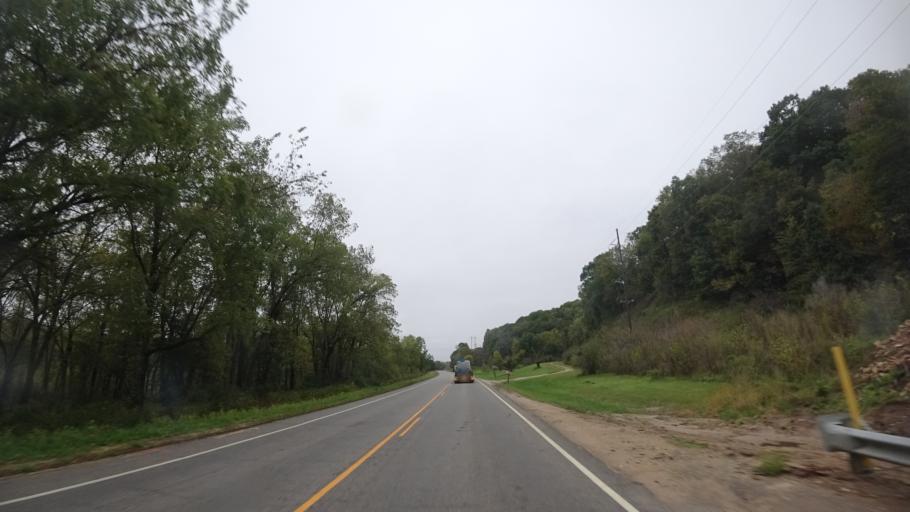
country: US
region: Wisconsin
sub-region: Crawford County
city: Prairie du Chien
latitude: 43.0681
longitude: -90.9473
